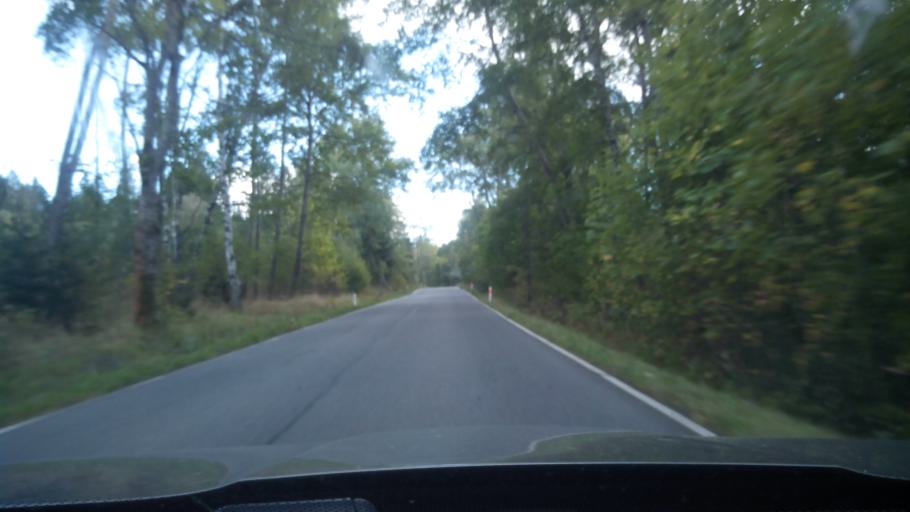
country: CZ
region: Plzensky
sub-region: Okres Klatovy
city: Kasperske Hory
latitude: 49.1386
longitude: 13.5800
